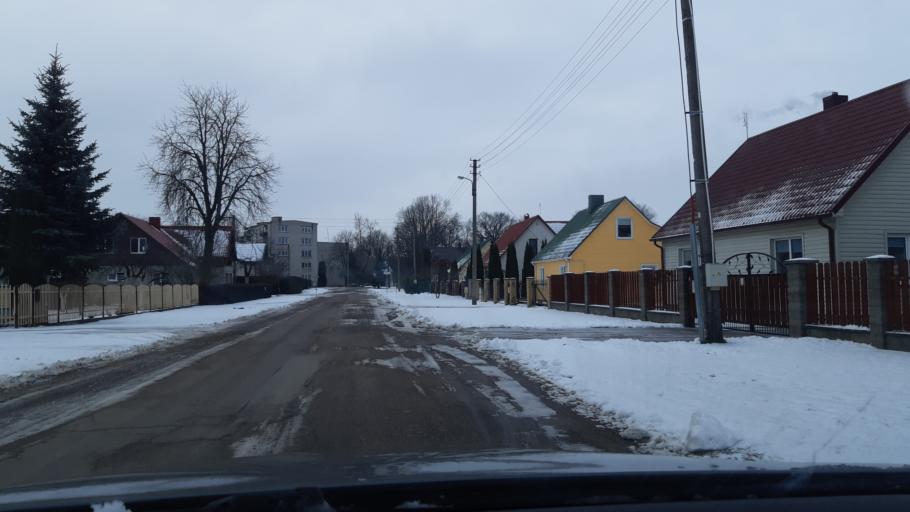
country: LT
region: Kauno apskritis
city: Kedainiai
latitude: 55.2933
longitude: 23.9797
